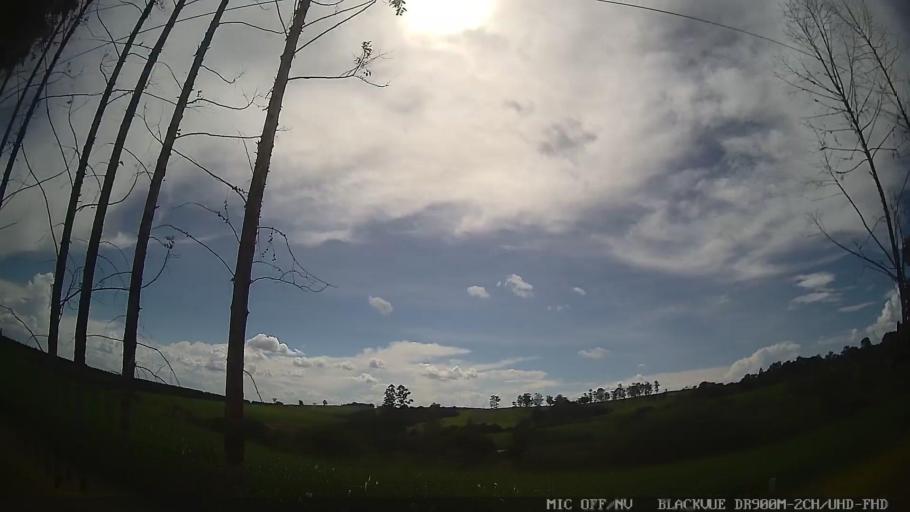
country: BR
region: Sao Paulo
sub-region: Conchas
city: Conchas
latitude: -22.9533
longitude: -47.9837
